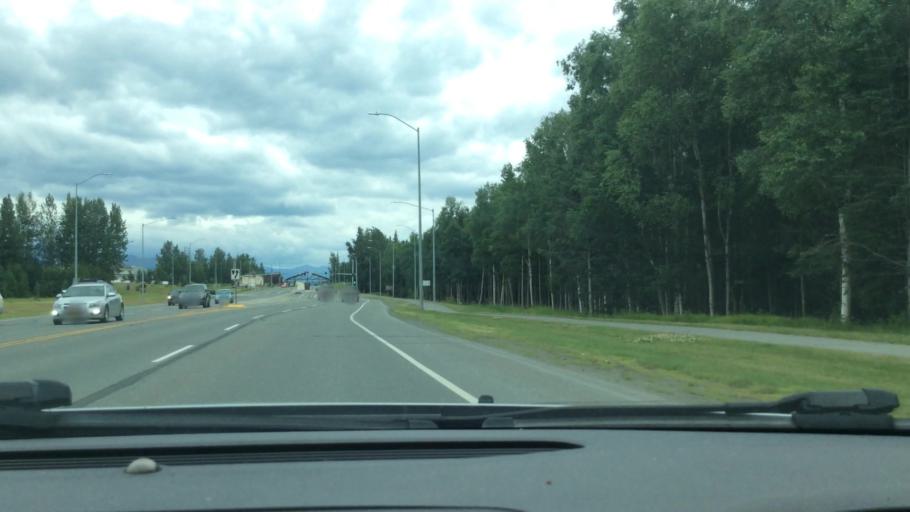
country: US
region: Alaska
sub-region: Anchorage Municipality
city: Anchorage
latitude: 61.2359
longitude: -149.7786
